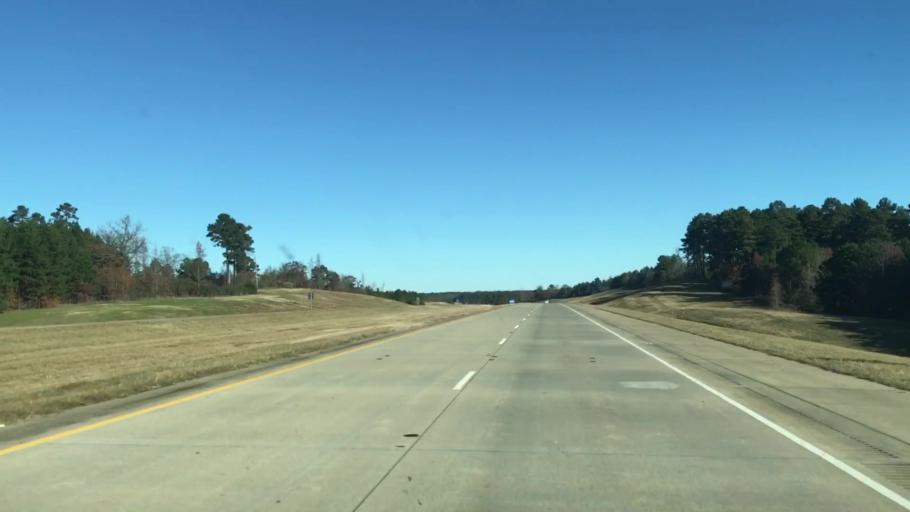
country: US
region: Louisiana
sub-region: Caddo Parish
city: Vivian
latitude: 33.0114
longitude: -93.9036
